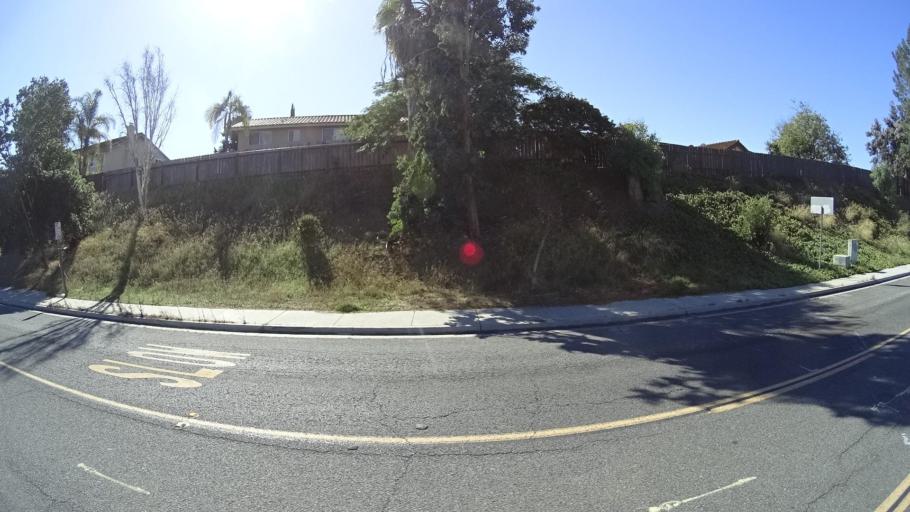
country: US
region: California
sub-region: San Diego County
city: Bonita
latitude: 32.6714
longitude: -117.0134
